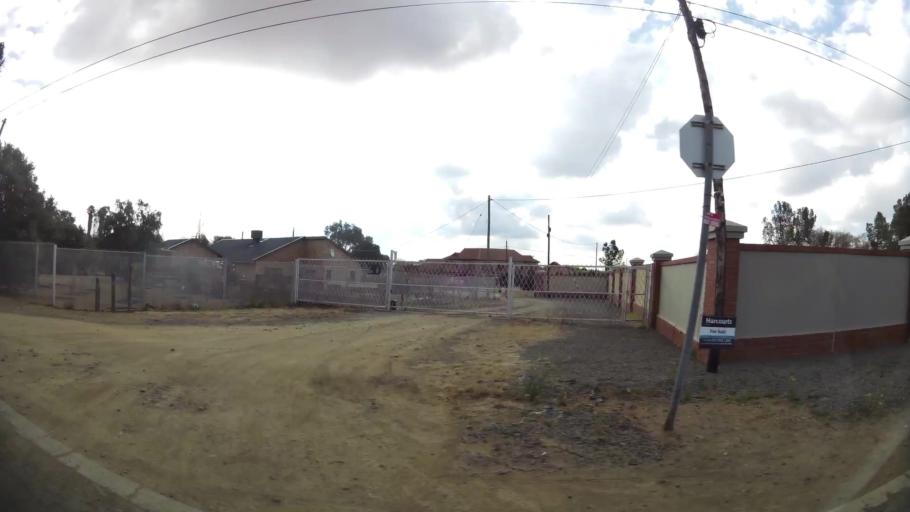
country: ZA
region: Orange Free State
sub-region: Mangaung Metropolitan Municipality
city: Bloemfontein
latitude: -29.0701
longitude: 26.1971
